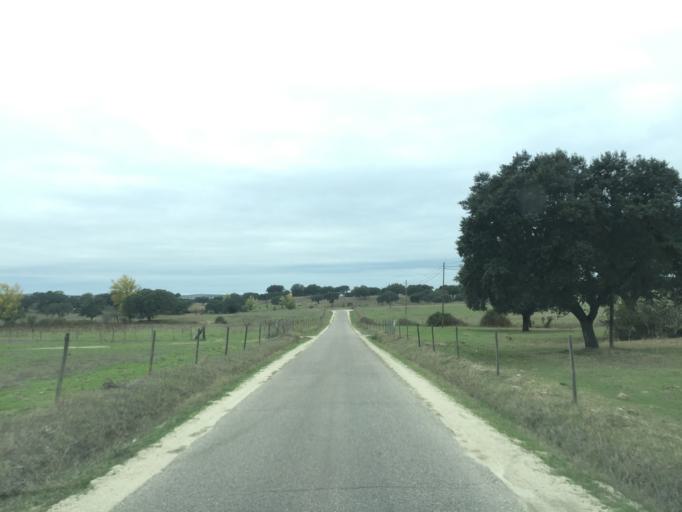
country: PT
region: Portalegre
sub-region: Fronteira
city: Vale da Amoreira
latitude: 39.0509
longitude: -7.7777
